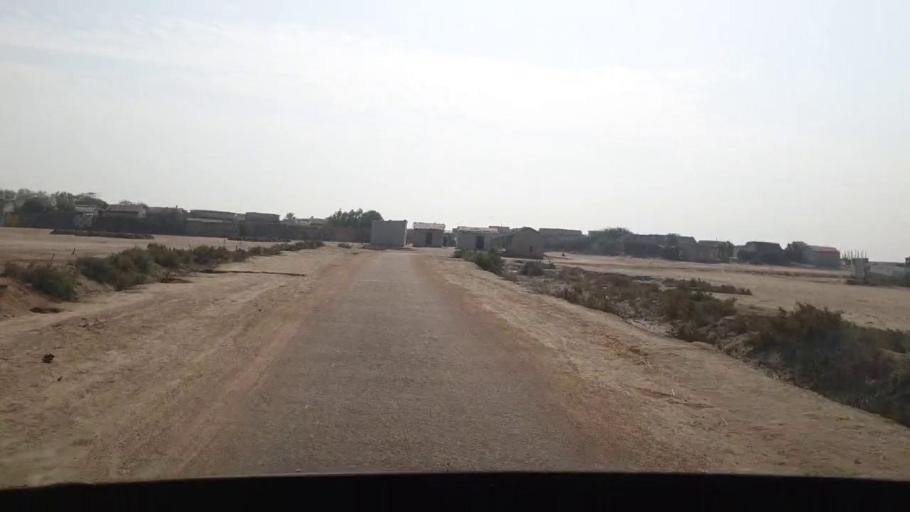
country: PK
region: Sindh
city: Chuhar Jamali
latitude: 24.2367
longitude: 67.9843
